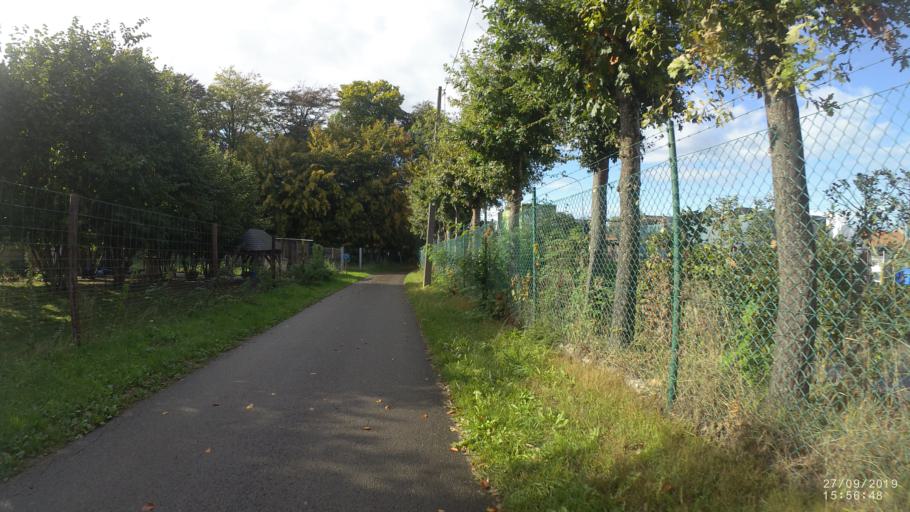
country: BE
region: Flanders
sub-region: Provincie Oost-Vlaanderen
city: Zottegem
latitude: 50.8693
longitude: 3.7559
